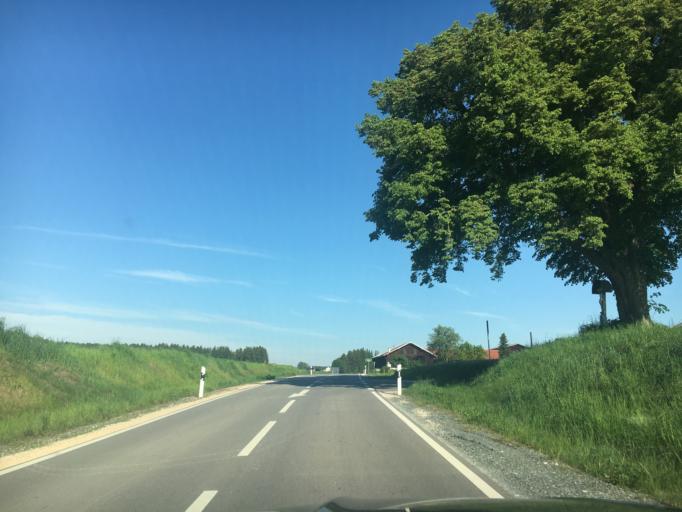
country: DE
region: Bavaria
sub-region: Upper Bavaria
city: Kirchweidach
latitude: 48.0664
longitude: 12.6114
